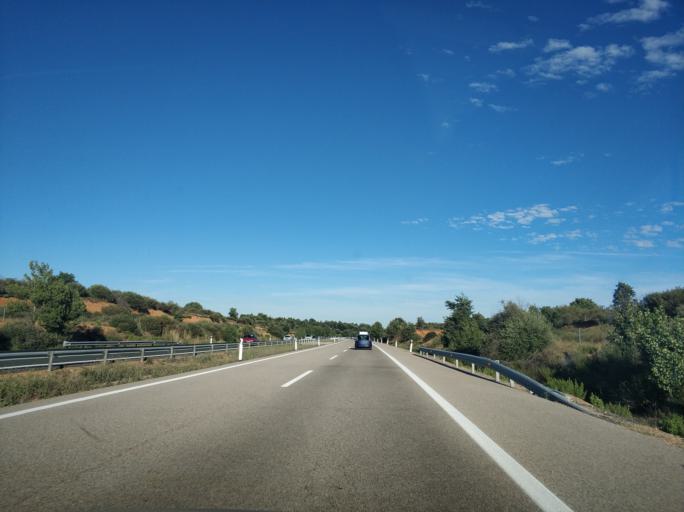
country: ES
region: Castille and Leon
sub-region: Provincia de Leon
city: Valverde de la Virgen
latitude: 42.6059
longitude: -5.7205
